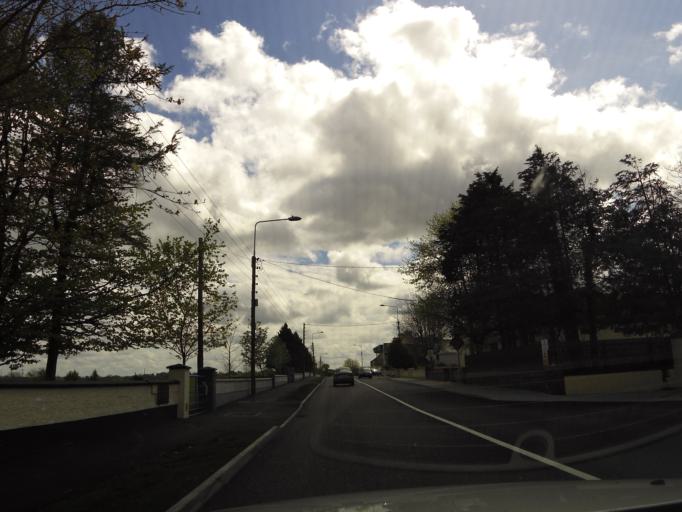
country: IE
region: Connaught
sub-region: County Galway
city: Tuam
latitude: 53.6122
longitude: -8.8976
